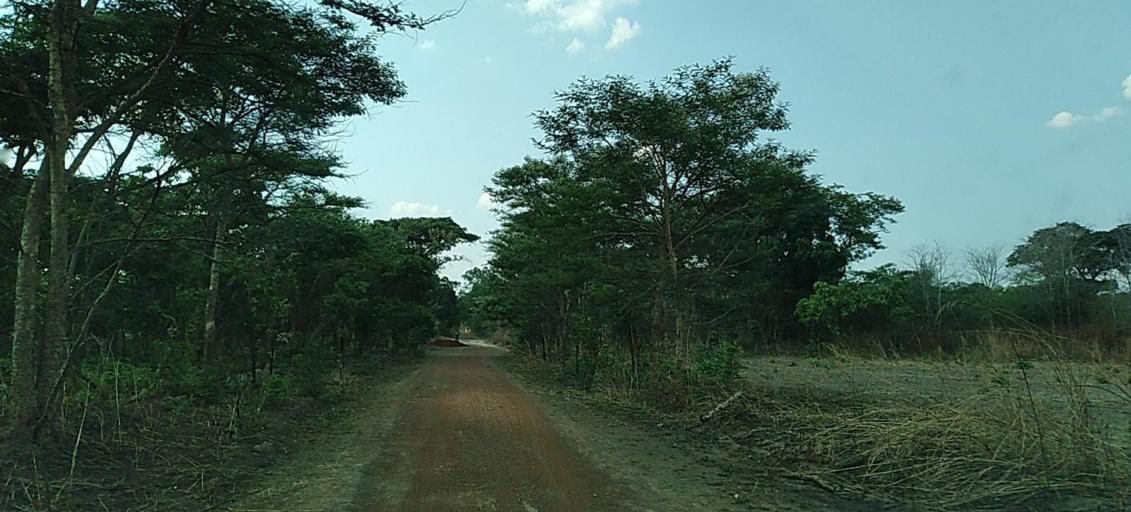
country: ZM
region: Copperbelt
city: Mpongwe
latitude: -13.4651
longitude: 28.0691
